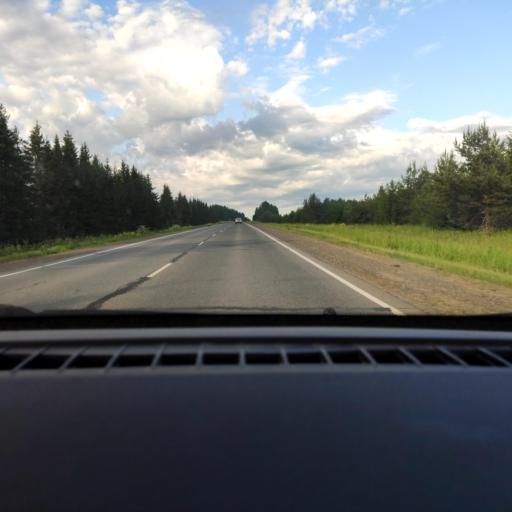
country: RU
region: Perm
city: Ocher
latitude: 57.4502
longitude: 54.4717
